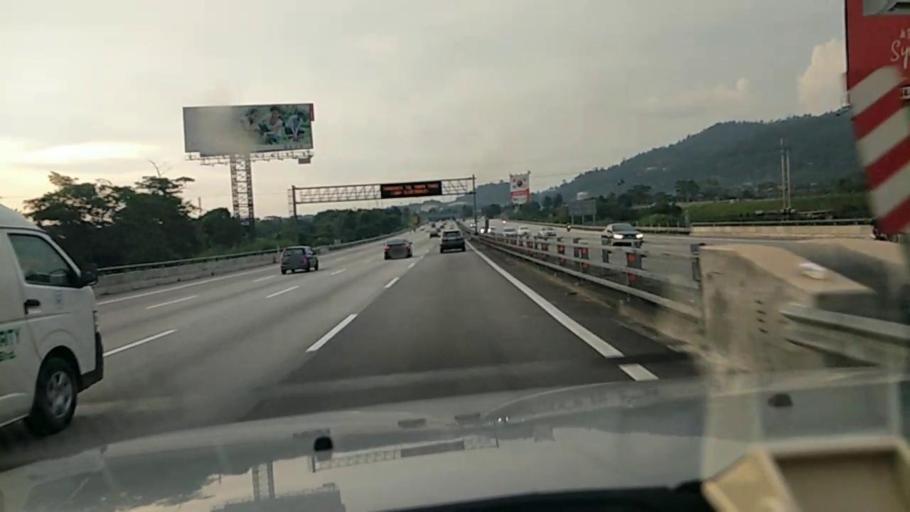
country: MY
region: Selangor
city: Kuang
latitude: 3.2168
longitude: 101.5803
